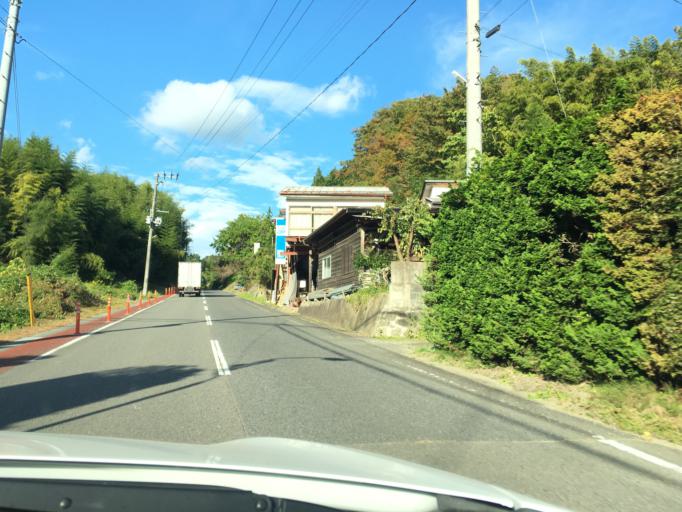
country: JP
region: Fukushima
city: Sukagawa
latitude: 37.2358
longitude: 140.4494
